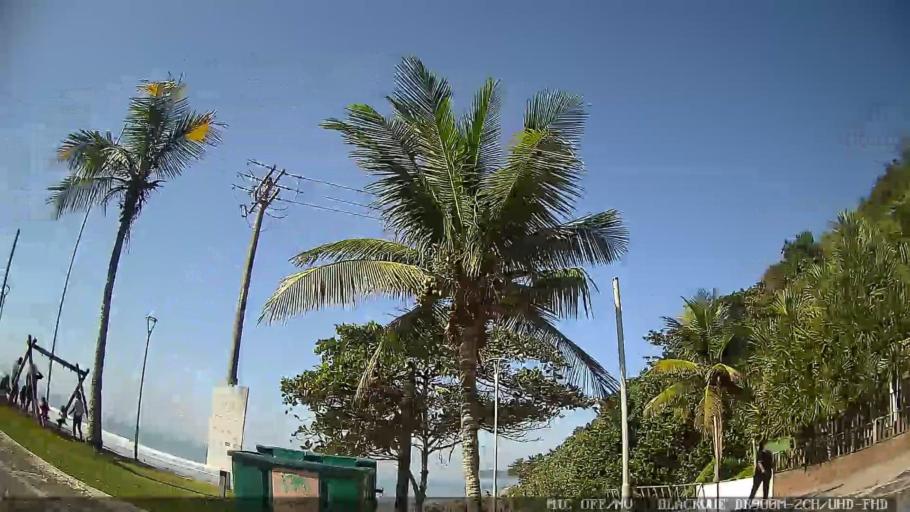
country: BR
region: Sao Paulo
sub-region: Guaruja
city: Guaruja
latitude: -24.0156
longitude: -46.2760
